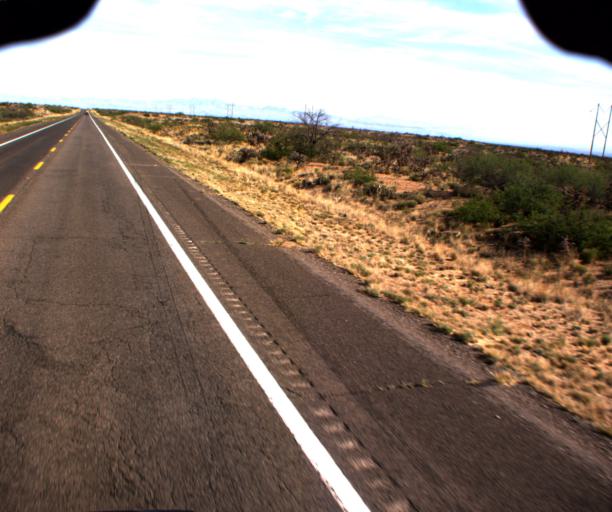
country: US
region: Arizona
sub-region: Graham County
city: Swift Trail Junction
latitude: 32.6112
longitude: -109.6875
